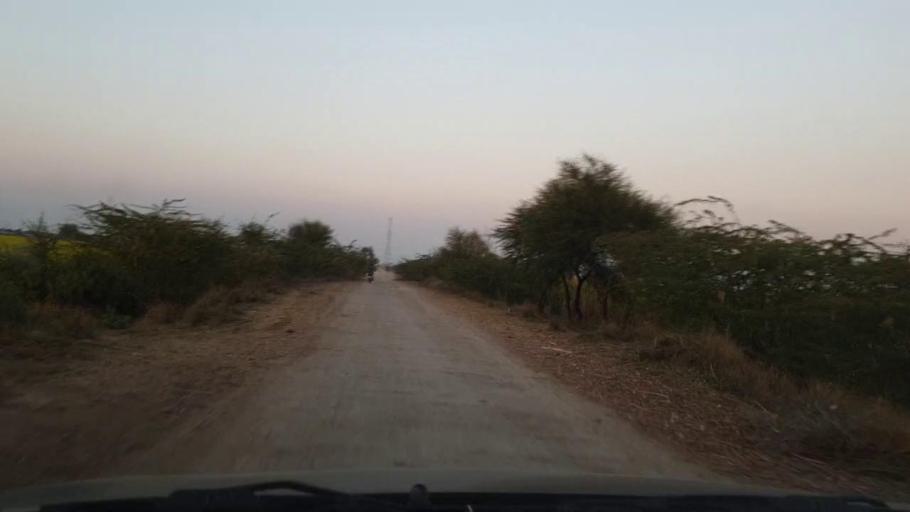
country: PK
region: Sindh
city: Jhol
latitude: 25.9463
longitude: 68.9747
